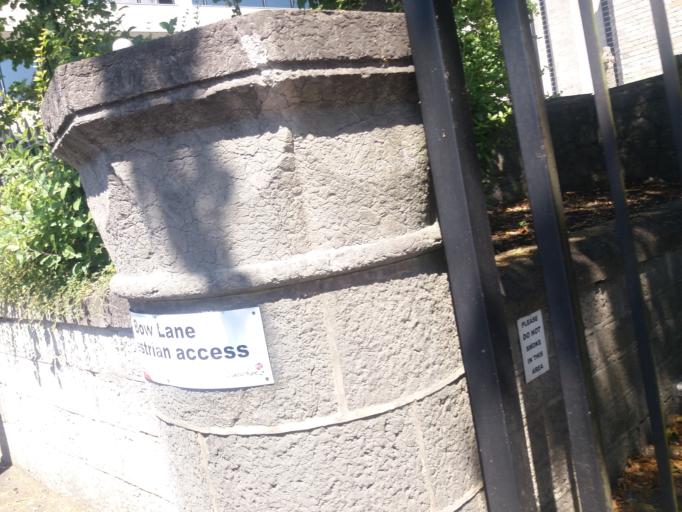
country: GB
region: England
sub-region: Lancashire
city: Preston
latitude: 53.7572
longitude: -2.7108
